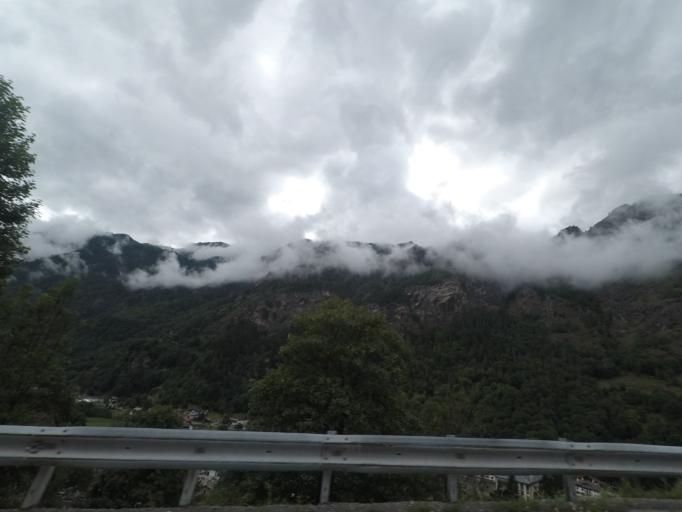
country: IT
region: Aosta Valley
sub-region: Valle d'Aosta
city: Valtournenche
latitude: 45.8667
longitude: 7.6182
